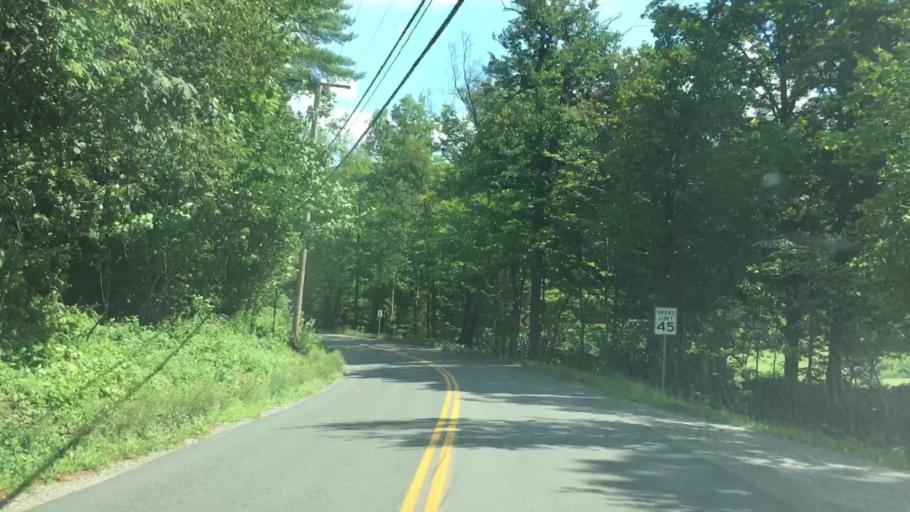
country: US
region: Vermont
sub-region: Windham County
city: West Brattleboro
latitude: 42.8013
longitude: -72.5984
